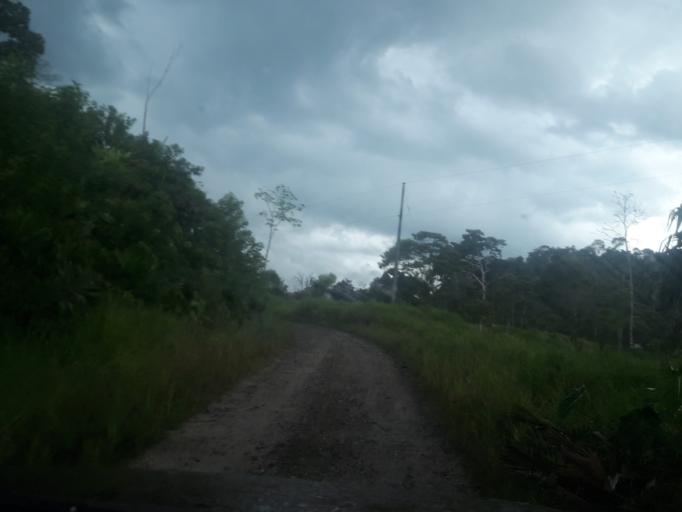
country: EC
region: Napo
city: Tena
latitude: -1.0856
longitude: -77.7087
